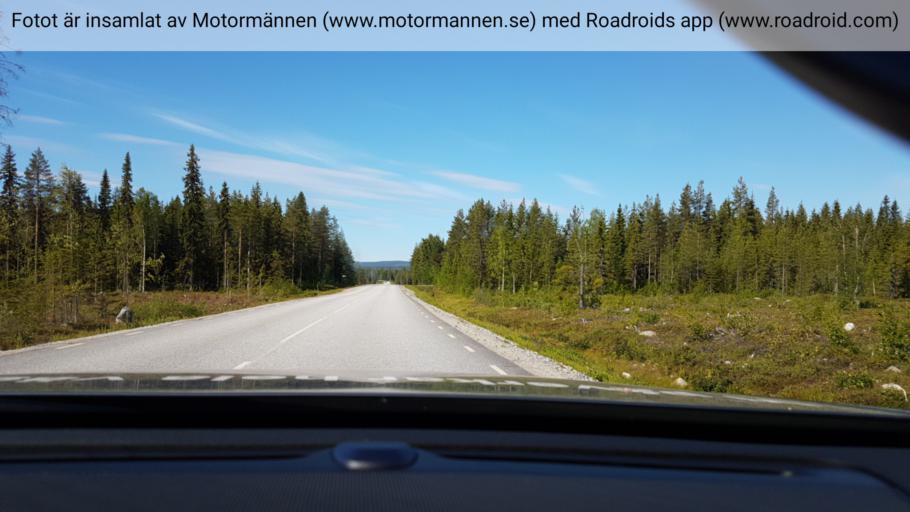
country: SE
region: Vaesterbotten
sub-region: Bjurholms Kommun
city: Bjurholm
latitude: 64.1670
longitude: 19.3845
